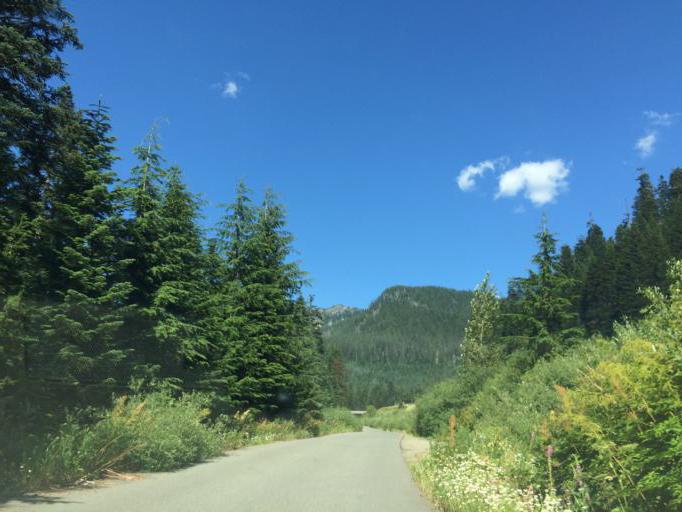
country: US
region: Washington
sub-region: King County
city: Tanner
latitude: 47.4277
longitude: -121.4261
